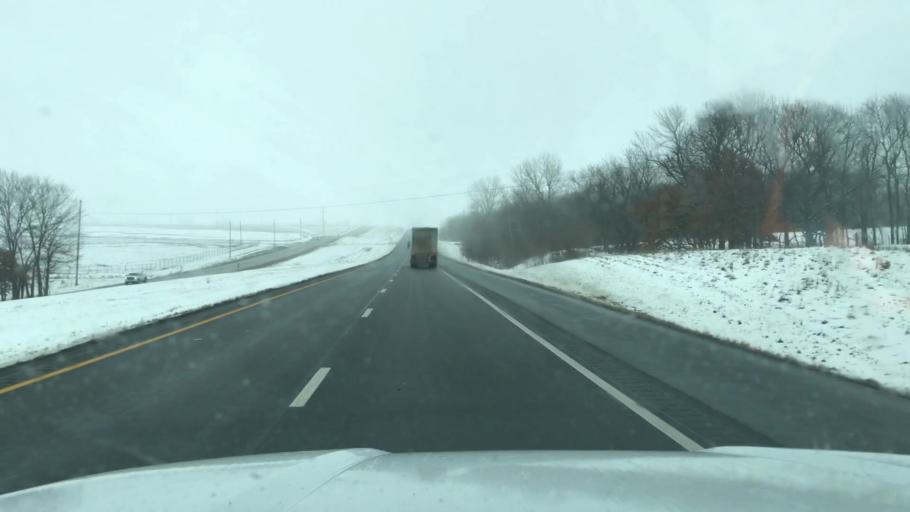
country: US
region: Missouri
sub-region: DeKalb County
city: Maysville
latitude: 39.7619
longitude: -94.4590
